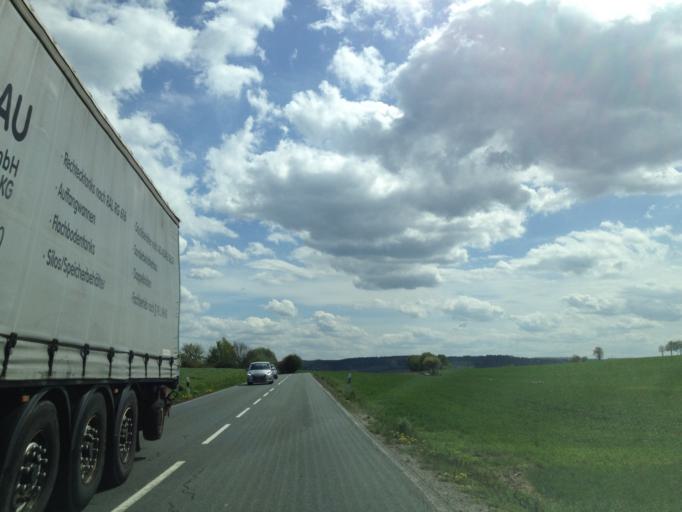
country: DE
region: North Rhine-Westphalia
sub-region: Regierungsbezirk Arnsberg
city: Mohnesee
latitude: 51.4964
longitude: 8.2110
